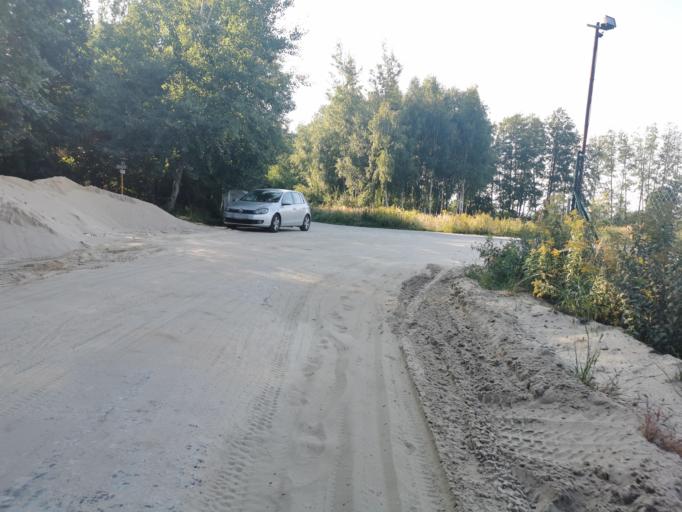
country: SK
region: Trnavsky
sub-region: Okres Senica
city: Senica
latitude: 48.6547
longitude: 17.3043
